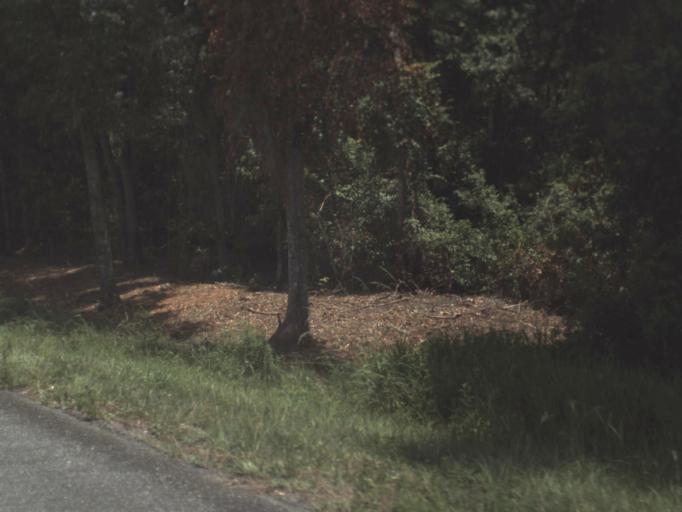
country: US
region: Florida
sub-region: Lafayette County
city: Mayo
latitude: 29.9691
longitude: -83.2174
